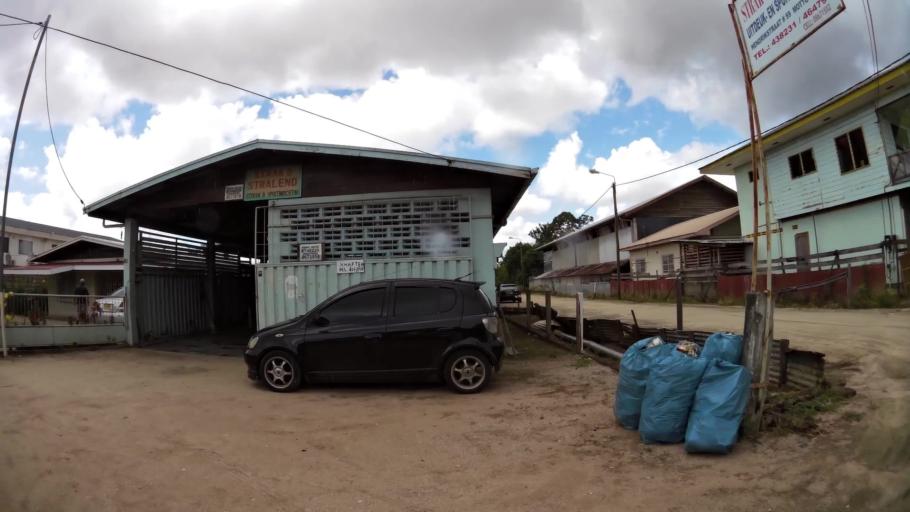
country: SR
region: Paramaribo
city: Paramaribo
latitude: 5.8329
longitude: -55.2079
